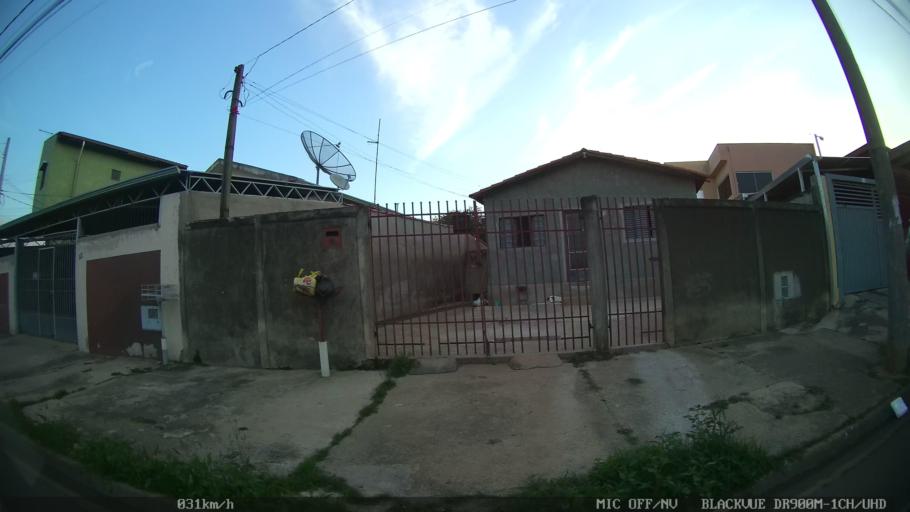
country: BR
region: Sao Paulo
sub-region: Hortolandia
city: Hortolandia
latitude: -22.8561
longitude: -47.2141
